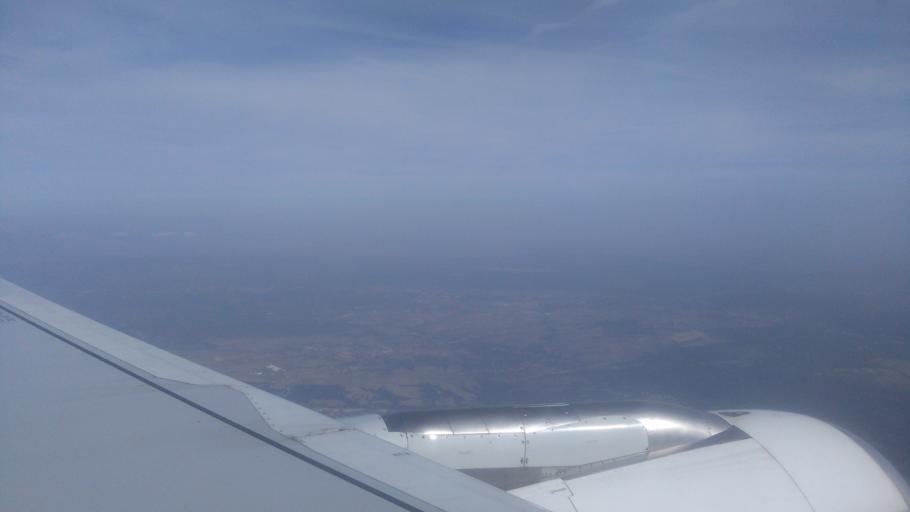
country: ES
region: Madrid
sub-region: Provincia de Madrid
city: Quijorna
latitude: 40.4043
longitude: -4.0603
